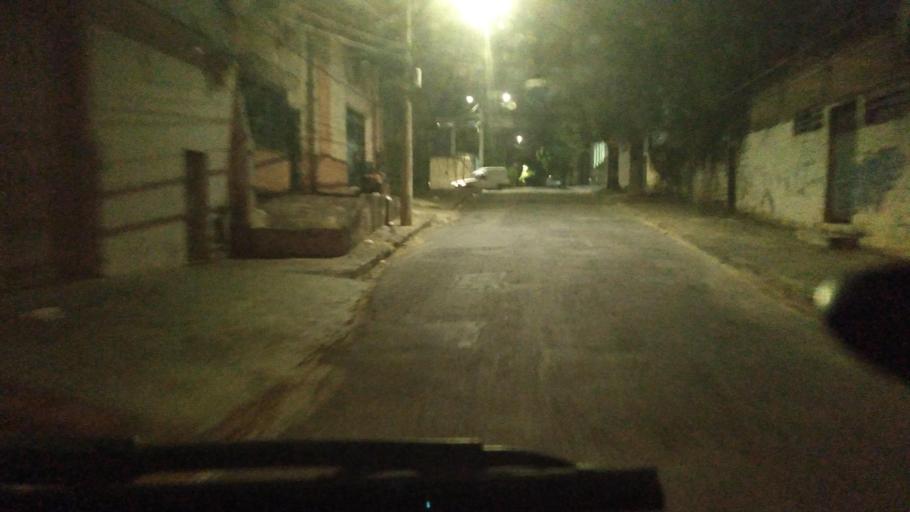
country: BR
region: Minas Gerais
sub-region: Belo Horizonte
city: Belo Horizonte
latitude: -19.8825
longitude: -43.9542
